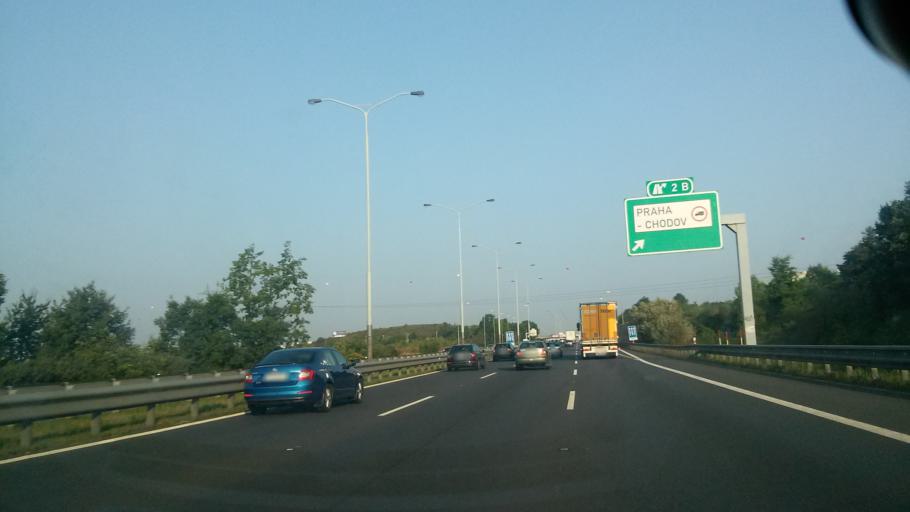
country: CZ
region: Central Bohemia
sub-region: Okres Praha-Zapad
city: Pruhonice
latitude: 50.0195
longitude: 14.5166
